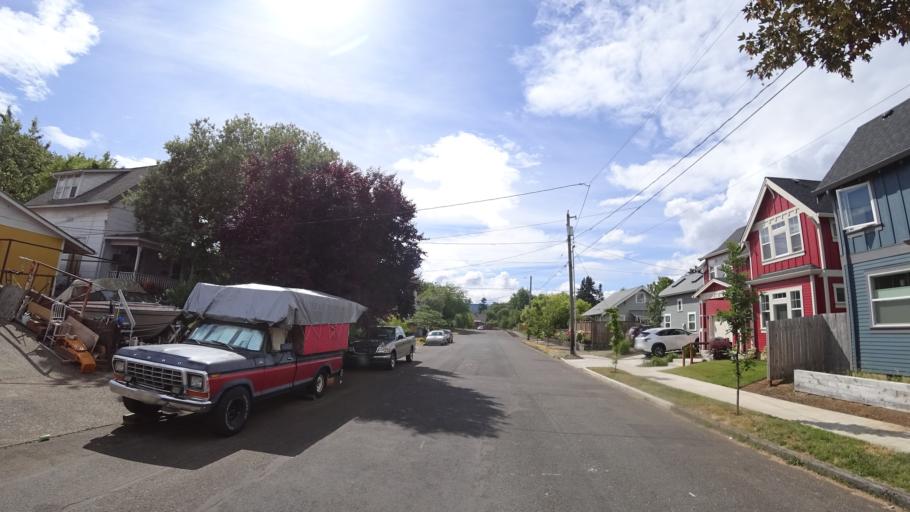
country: US
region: Oregon
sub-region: Washington County
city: West Haven
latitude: 45.5921
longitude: -122.7482
